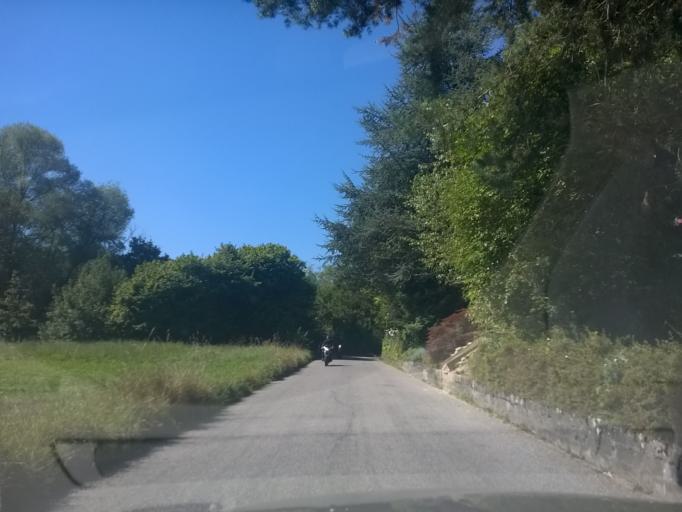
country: CH
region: Zurich
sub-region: Bezirk Winterthur
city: Wuelflingen (Kreis 6) / Niederfeld
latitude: 47.5007
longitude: 8.6719
